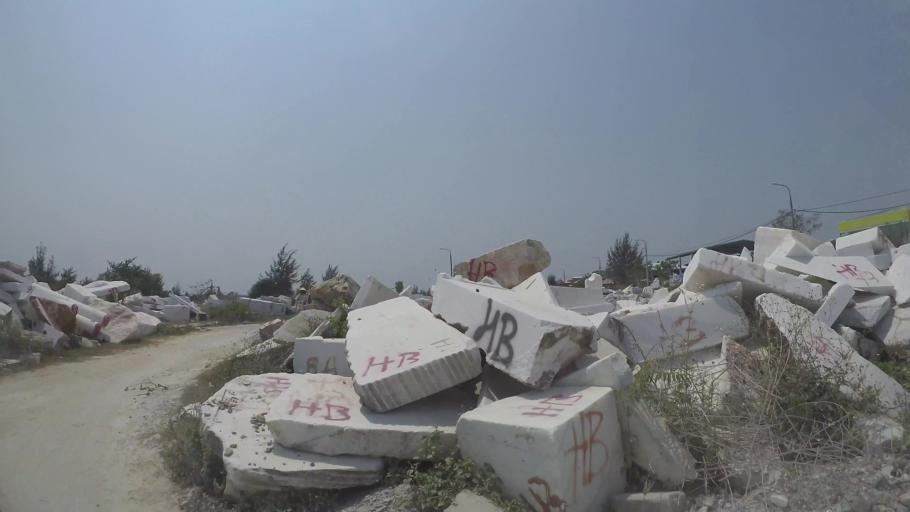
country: VN
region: Da Nang
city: Ngu Hanh Son
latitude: 15.9887
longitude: 108.2521
